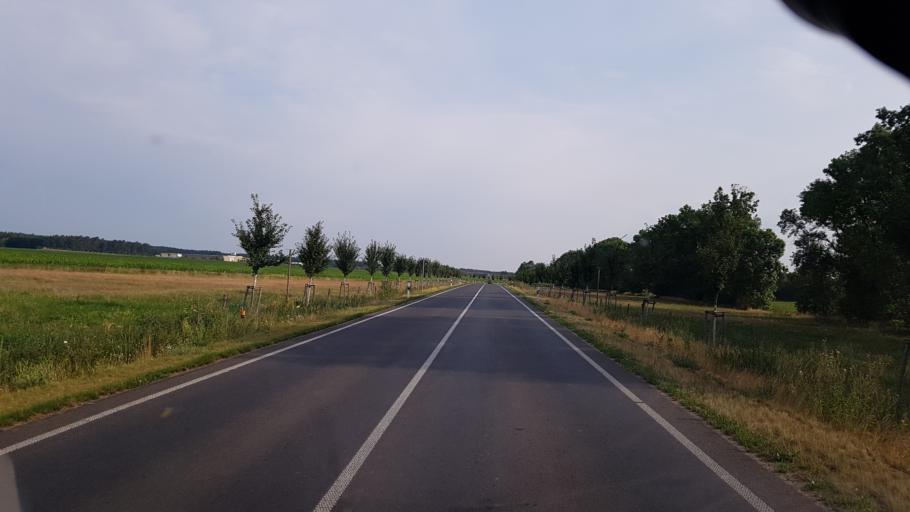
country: DE
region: Brandenburg
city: Golssen
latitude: 51.9728
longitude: 13.5714
